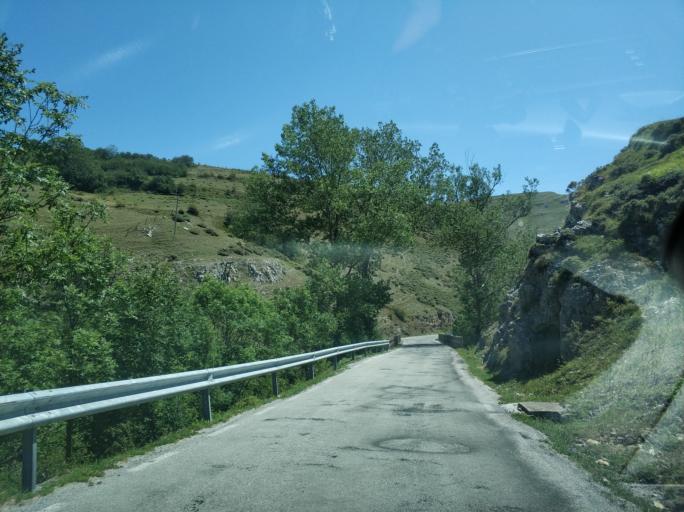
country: ES
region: Cantabria
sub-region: Provincia de Cantabria
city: Reinosa
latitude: 43.0319
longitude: -4.1720
